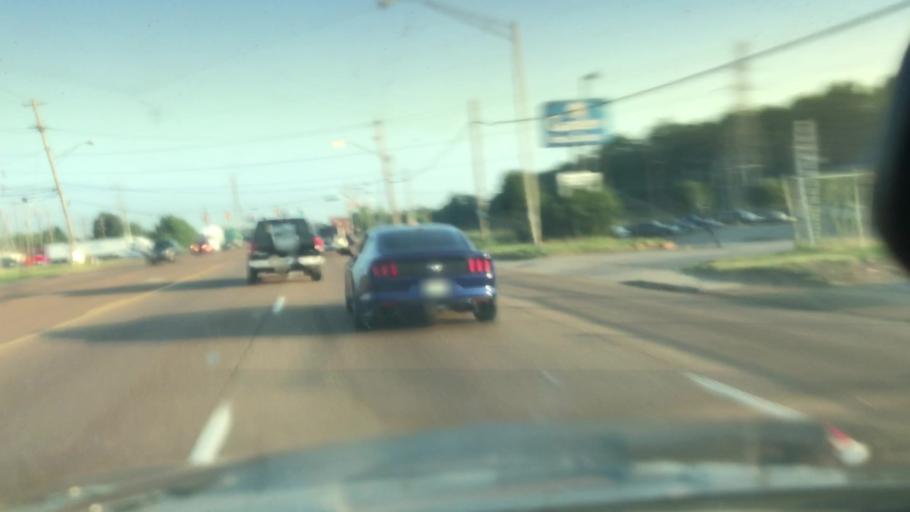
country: US
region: Mississippi
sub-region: De Soto County
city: Southaven
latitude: 35.0755
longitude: -89.9498
